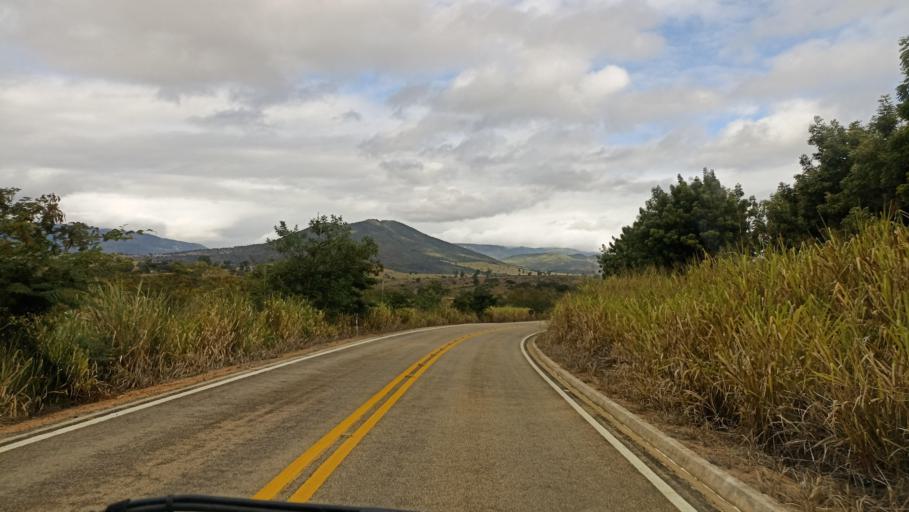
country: BR
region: Minas Gerais
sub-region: Joaima
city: Joaima
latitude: -16.6949
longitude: -40.9565
